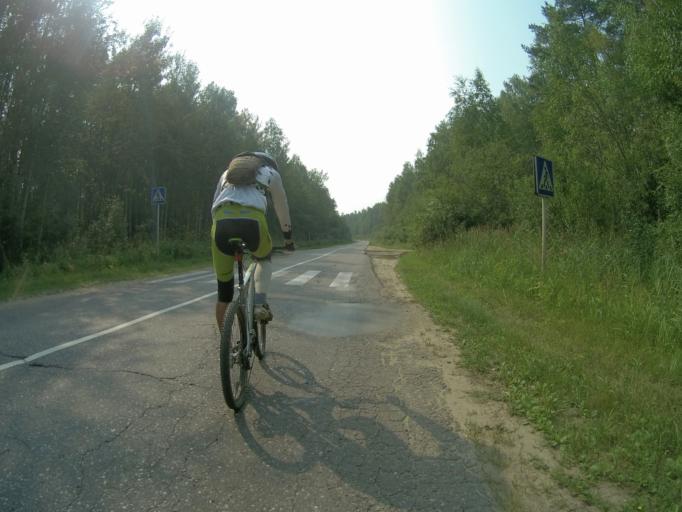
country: RU
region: Vladimir
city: Vorsha
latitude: 56.0094
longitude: 40.1218
